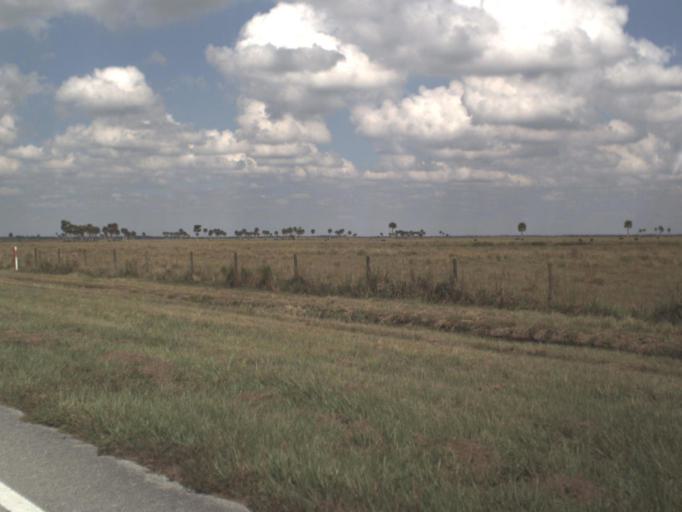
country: US
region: Florida
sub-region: Okeechobee County
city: Okeechobee
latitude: 27.3357
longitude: -80.9345
